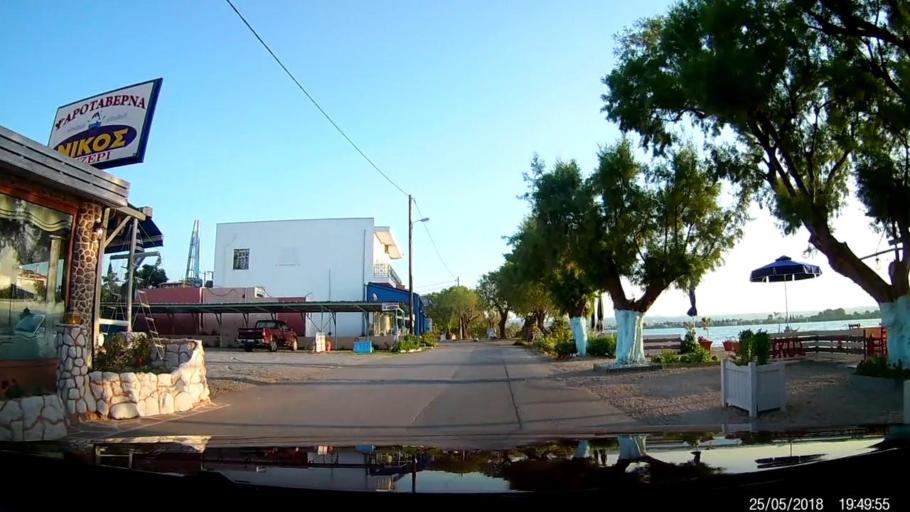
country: GR
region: Central Greece
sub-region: Nomos Evvoias
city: Ayios Nikolaos
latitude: 38.4088
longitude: 23.6401
